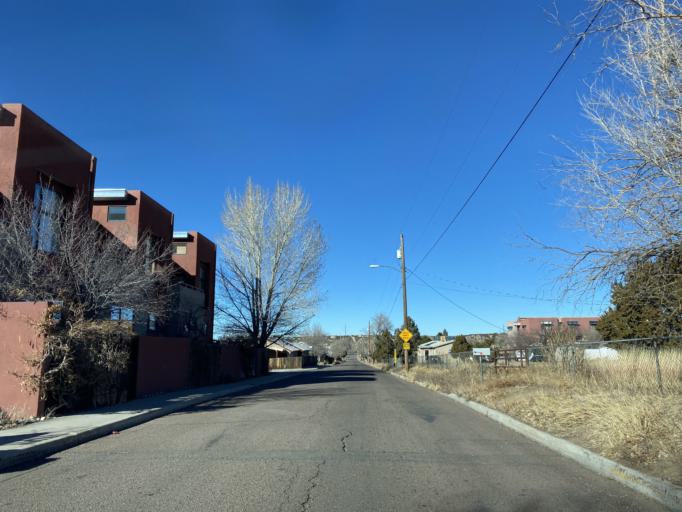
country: US
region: New Mexico
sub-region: Santa Fe County
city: Agua Fria
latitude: 35.6593
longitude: -105.9878
